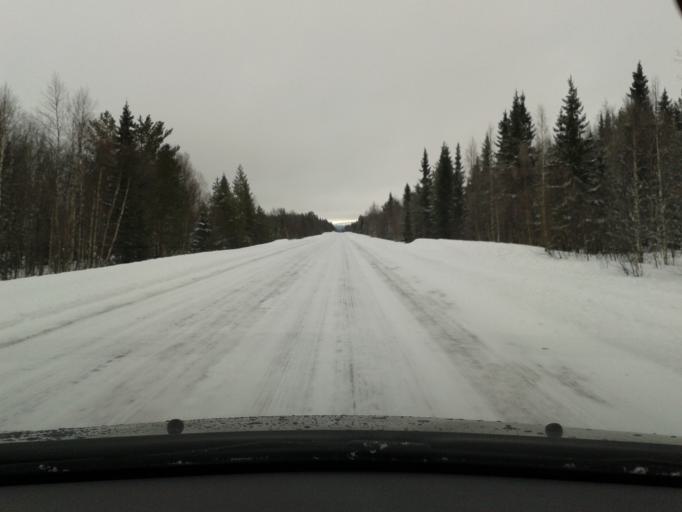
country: SE
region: Vaesterbotten
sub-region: Vilhelmina Kommun
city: Sjoberg
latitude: 64.8500
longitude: 15.9080
